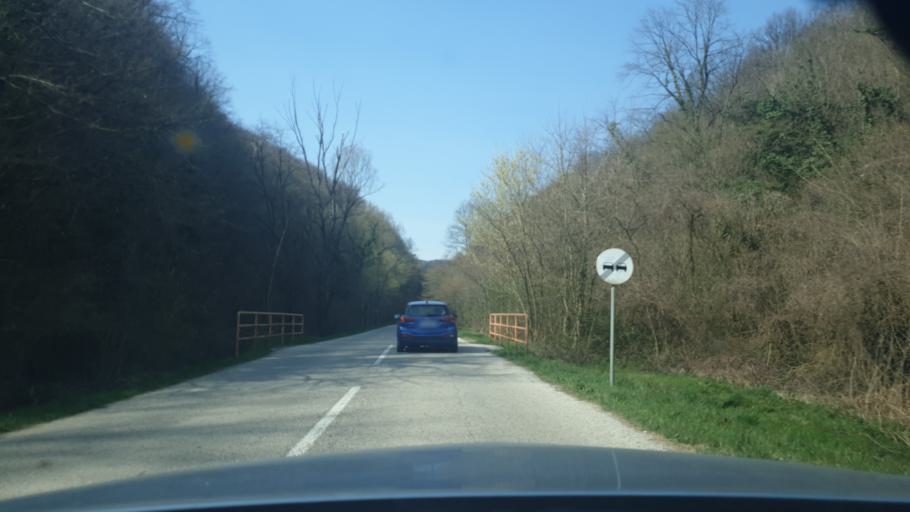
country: RS
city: Vrdnik
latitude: 45.1408
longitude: 19.7737
